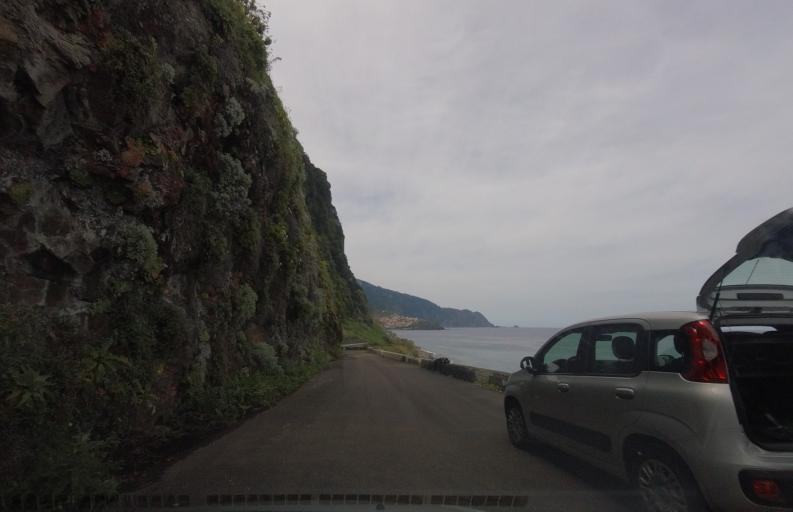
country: PT
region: Madeira
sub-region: Sao Vicente
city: Sao Vicente
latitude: 32.8139
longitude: -17.0760
